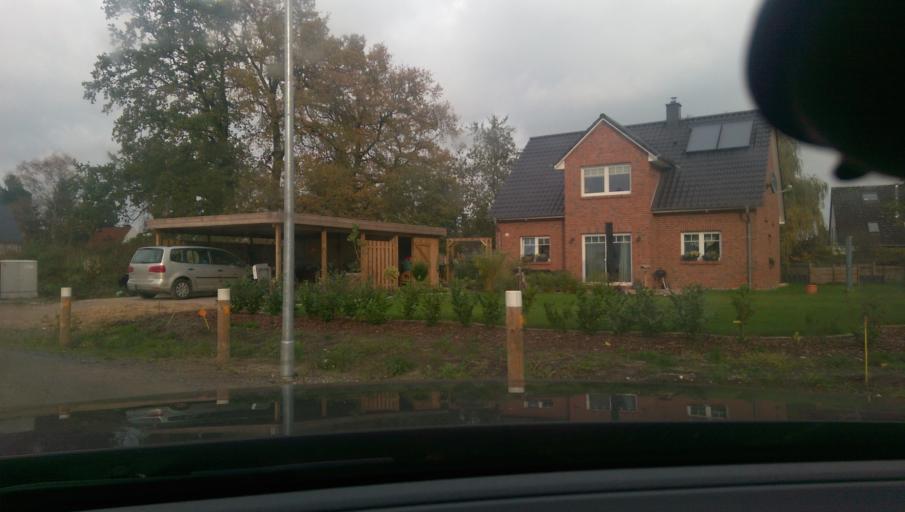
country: DE
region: Lower Saxony
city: Elze
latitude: 52.5763
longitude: 9.7322
